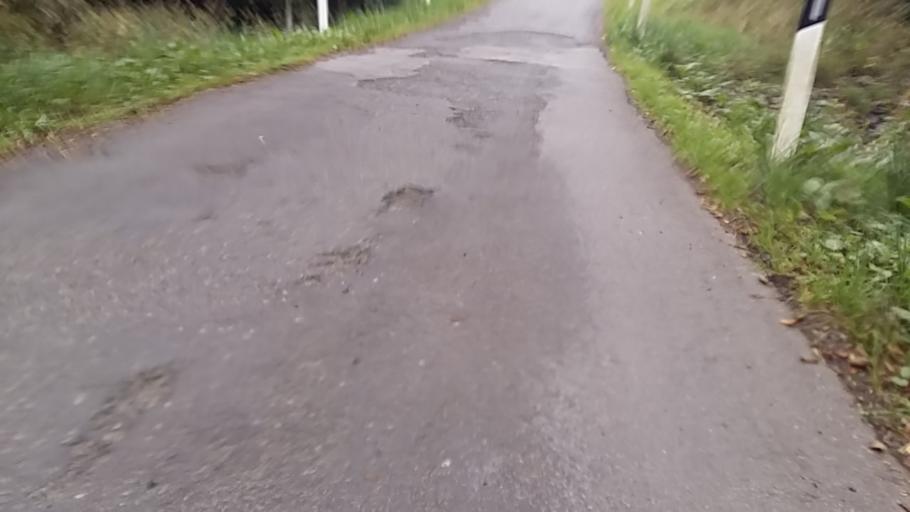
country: SE
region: Joenkoeping
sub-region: Jonkopings Kommun
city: Taberg
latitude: 57.7068
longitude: 14.1111
